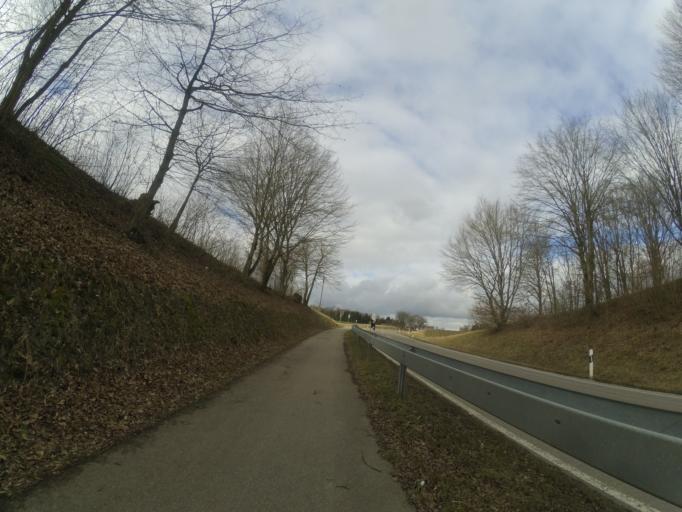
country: DE
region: Bavaria
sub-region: Swabia
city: Bellenberg
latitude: 48.2782
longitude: 10.1189
